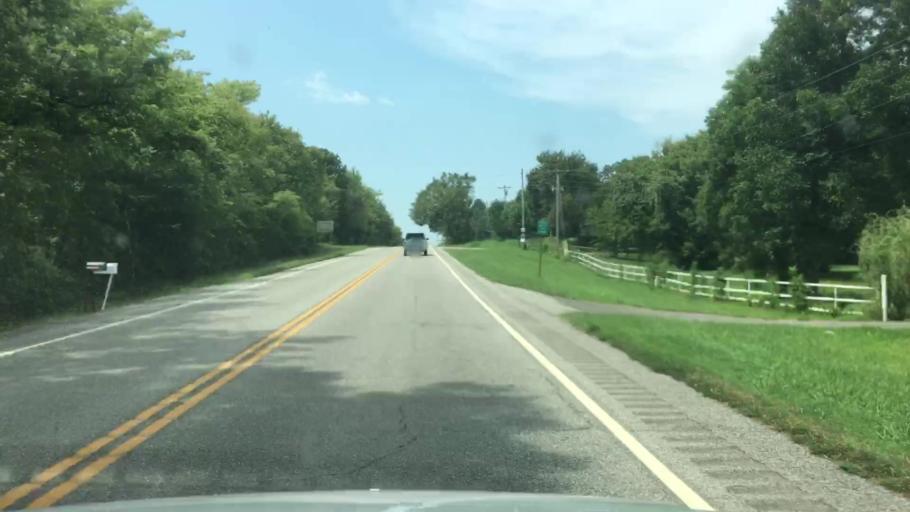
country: US
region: Oklahoma
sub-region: Wagoner County
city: Wagoner
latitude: 35.9297
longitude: -95.2421
